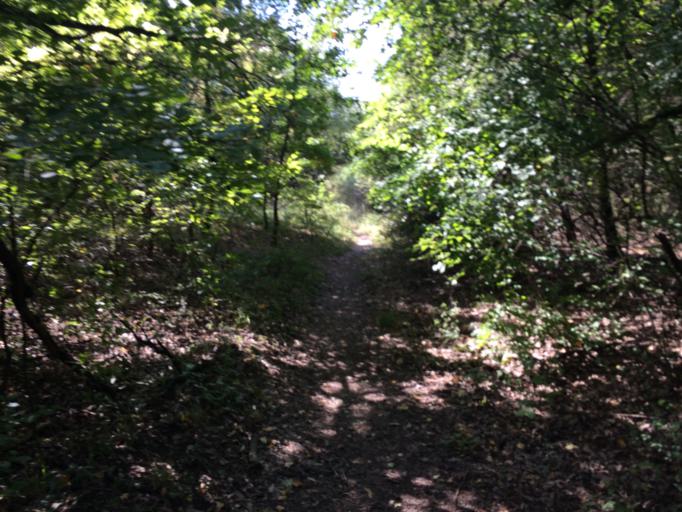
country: HU
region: Pest
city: Nagymaros
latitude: 47.8241
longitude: 18.9444
